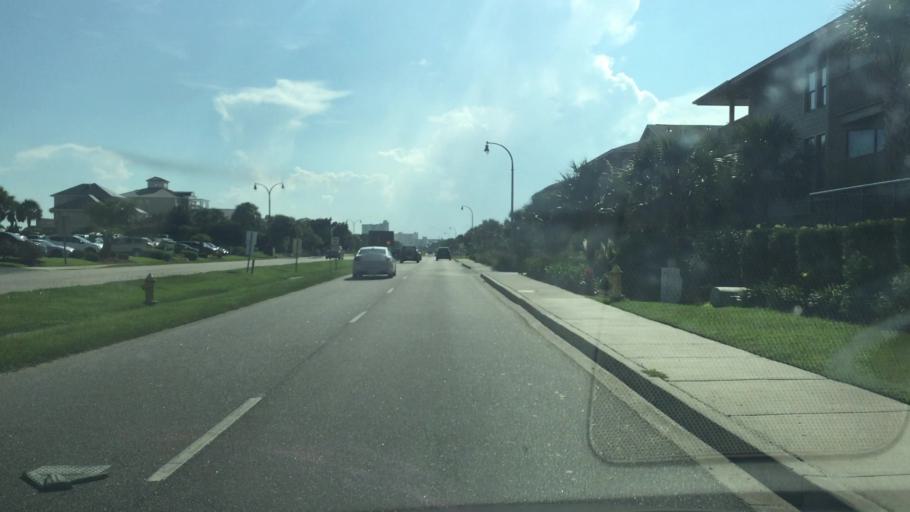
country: US
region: South Carolina
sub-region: Horry County
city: North Myrtle Beach
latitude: 33.8219
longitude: -78.6693
